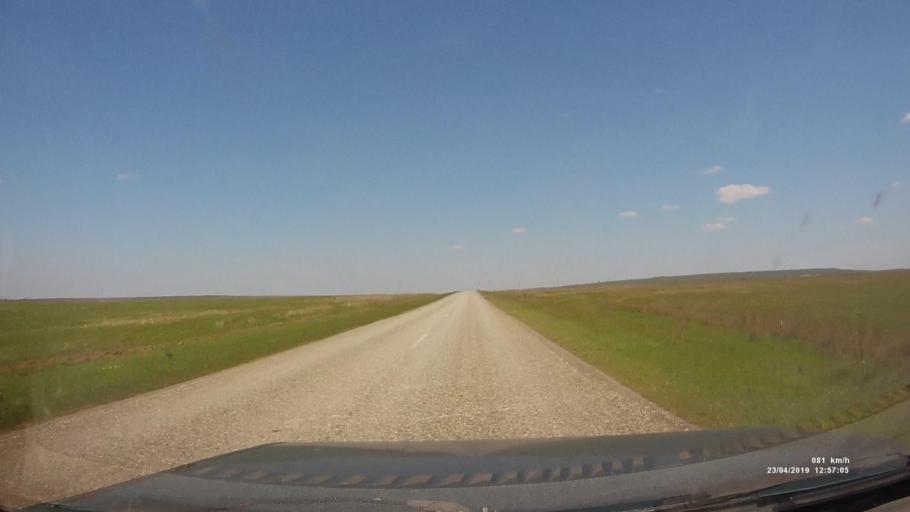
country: RU
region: Kalmykiya
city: Yashalta
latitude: 46.6006
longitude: 42.5781
